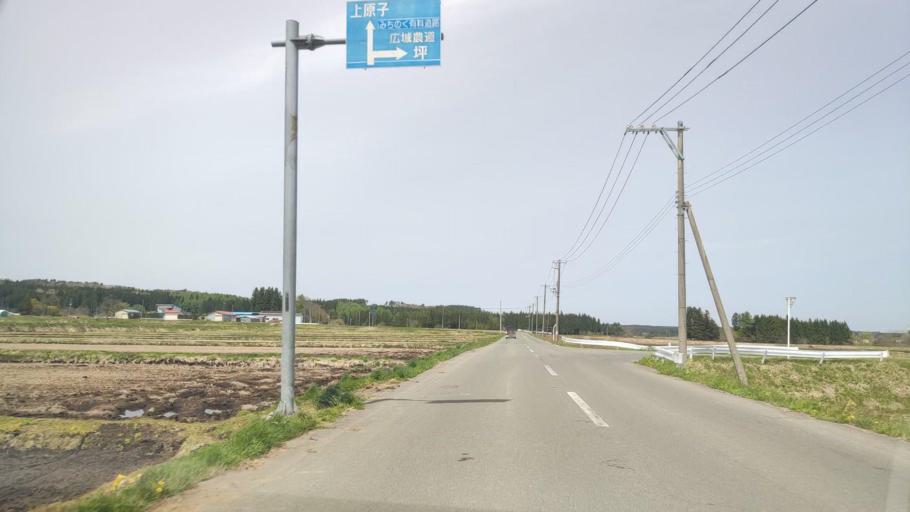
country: JP
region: Aomori
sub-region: Misawa Shi
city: Inuotose
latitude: 40.7612
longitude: 141.1196
